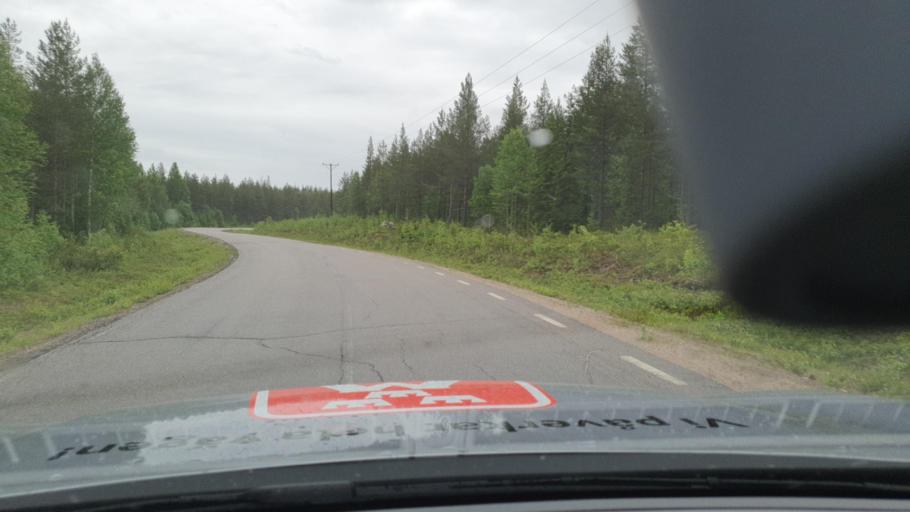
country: SE
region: Norrbotten
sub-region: Pajala Kommun
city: Pajala
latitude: 66.7677
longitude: 23.1498
